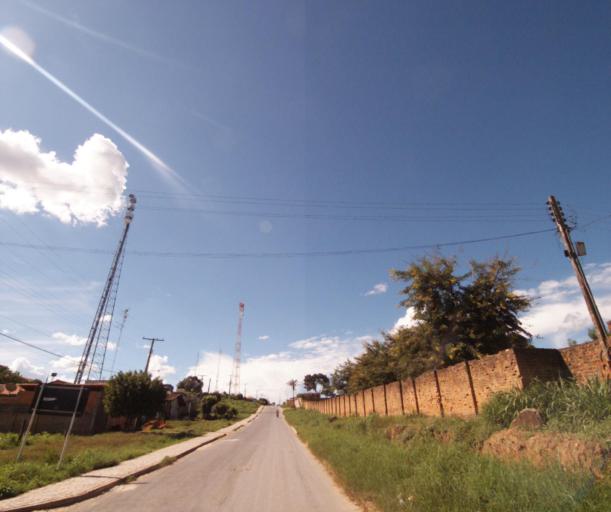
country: BR
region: Bahia
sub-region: Correntina
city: Correntina
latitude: -13.3382
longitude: -44.6366
